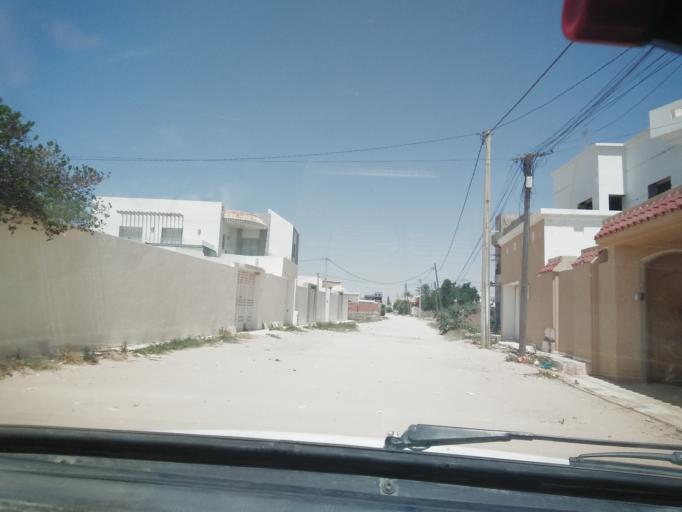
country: TN
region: Safaqis
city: Al Qarmadah
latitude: 34.8043
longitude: 10.7749
